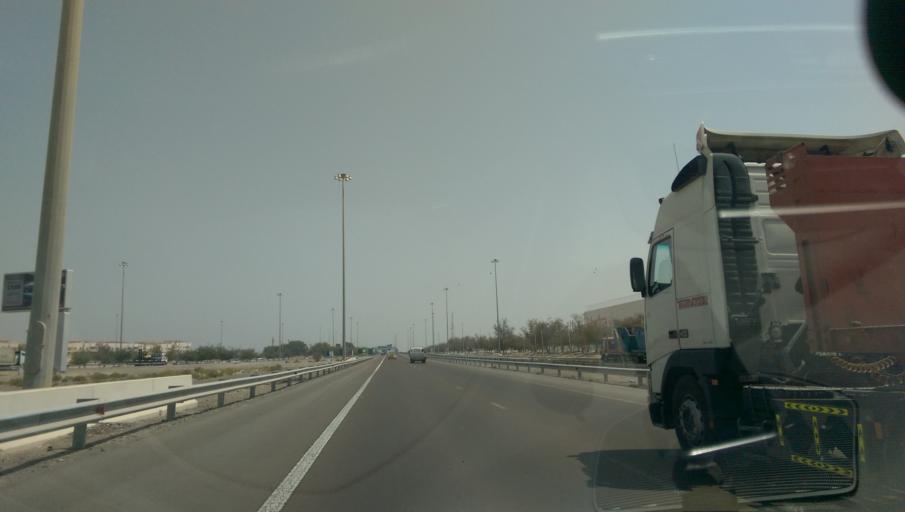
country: AE
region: Abu Dhabi
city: Abu Dhabi
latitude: 24.5460
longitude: 54.6939
